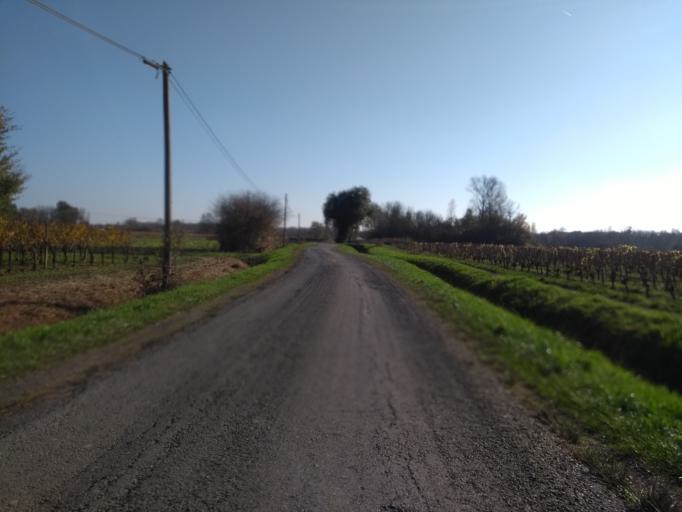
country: FR
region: Aquitaine
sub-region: Departement de la Gironde
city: Cambes
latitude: 44.7247
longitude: -0.4688
